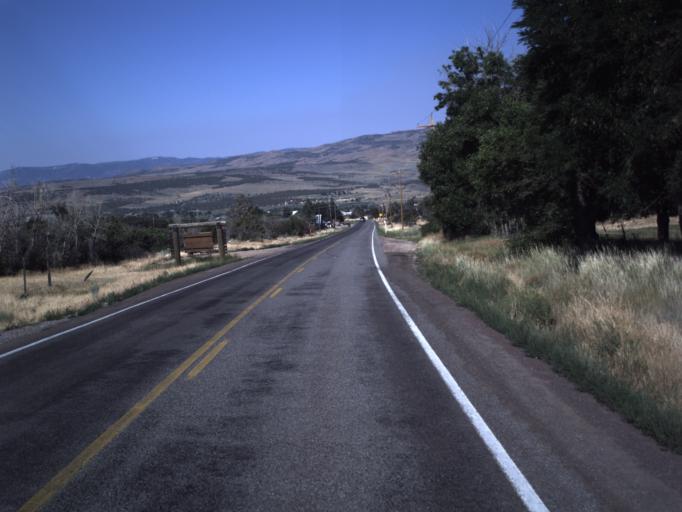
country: US
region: Utah
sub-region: Sanpete County
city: Fairview
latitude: 39.6436
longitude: -111.4117
